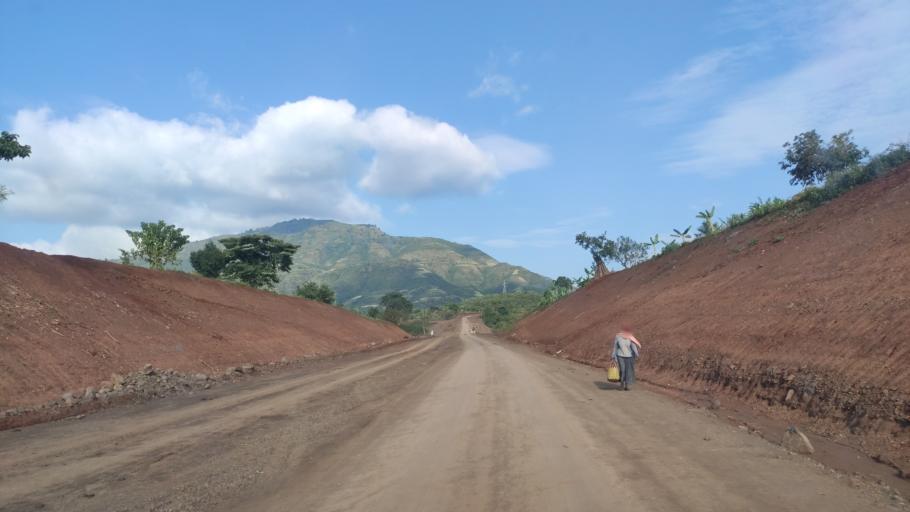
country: ET
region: Southern Nations, Nationalities, and People's Region
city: Arba Minch'
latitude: 6.4264
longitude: 37.3223
